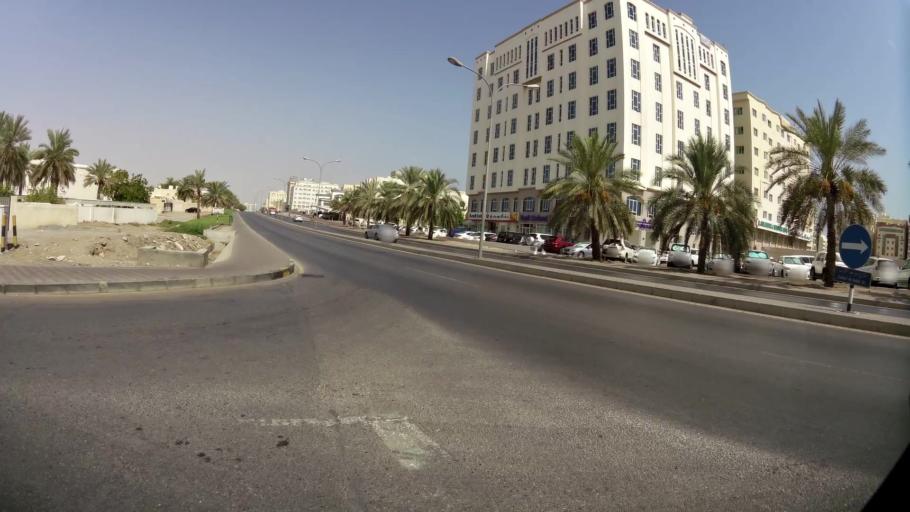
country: OM
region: Muhafazat Masqat
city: Bawshar
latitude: 23.5931
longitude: 58.4275
